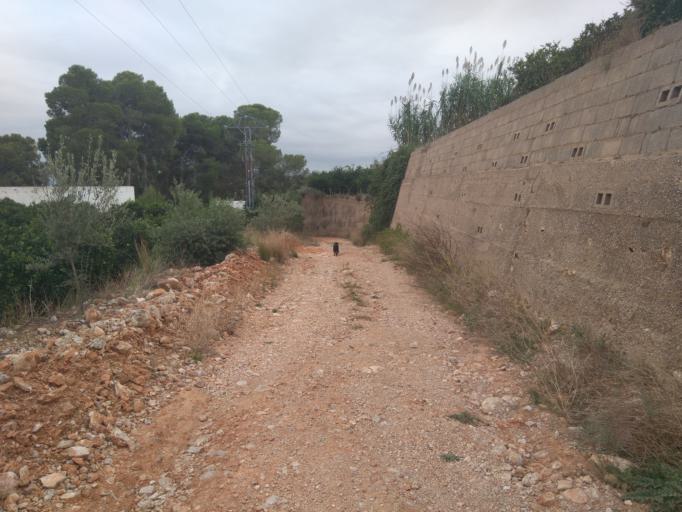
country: ES
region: Valencia
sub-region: Provincia de Valencia
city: Benimodo
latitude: 39.1944
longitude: -0.5692
